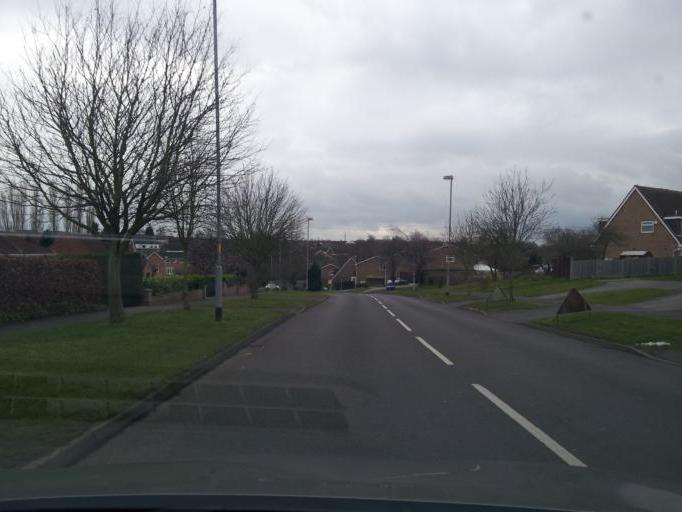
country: GB
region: England
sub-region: Lincolnshire
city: Great Gonerby
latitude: 52.9130
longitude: -0.6679
